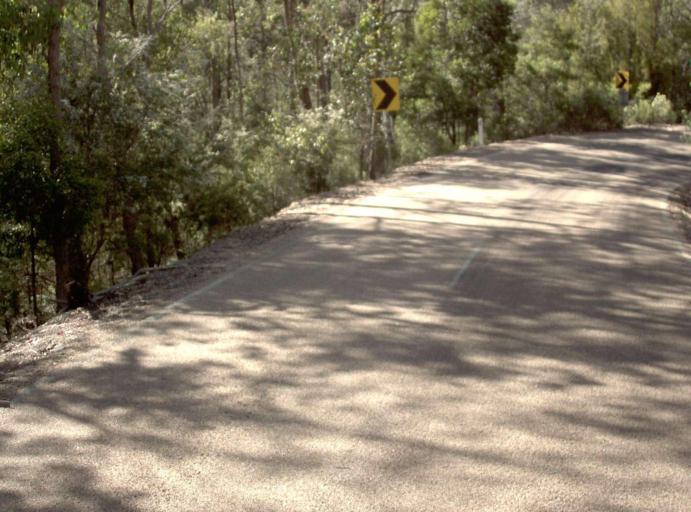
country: AU
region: Victoria
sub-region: East Gippsland
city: Lakes Entrance
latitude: -37.5015
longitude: 148.5508
